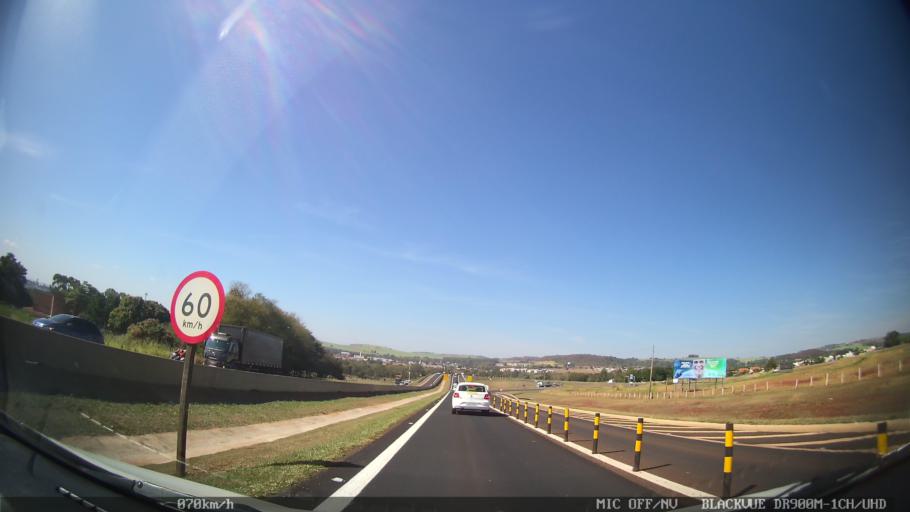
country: BR
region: Sao Paulo
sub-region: Ribeirao Preto
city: Ribeirao Preto
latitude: -21.2222
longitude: -47.7795
